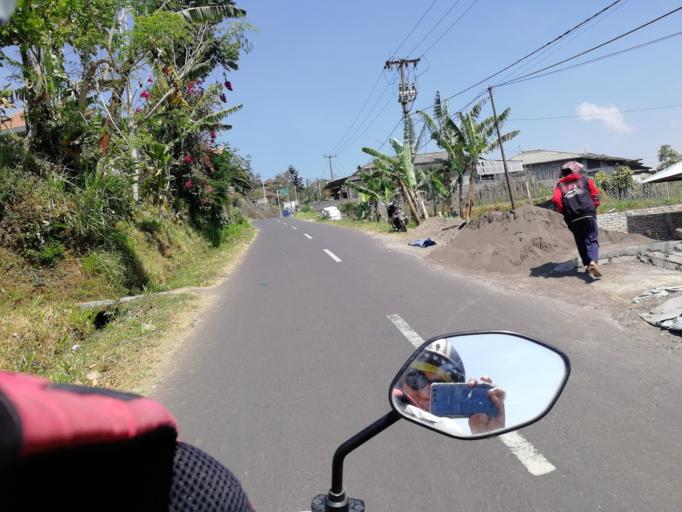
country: ID
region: Bali
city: Peneng
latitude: -8.3001
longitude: 115.1798
